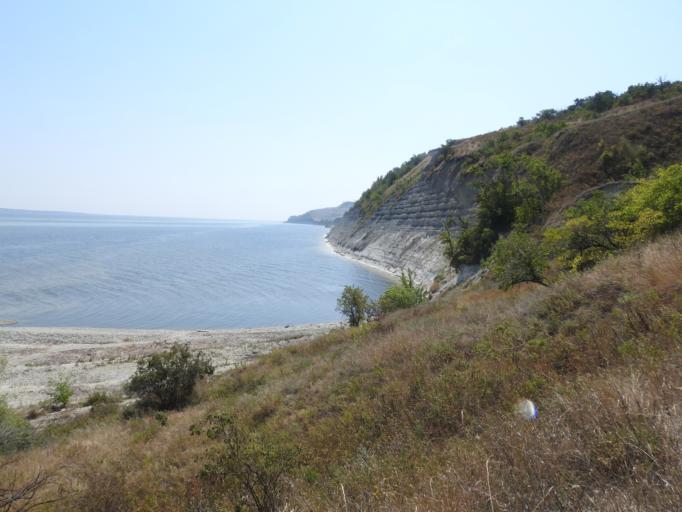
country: RU
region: Saratov
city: Kamenskiy
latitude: 50.5923
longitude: 45.6931
